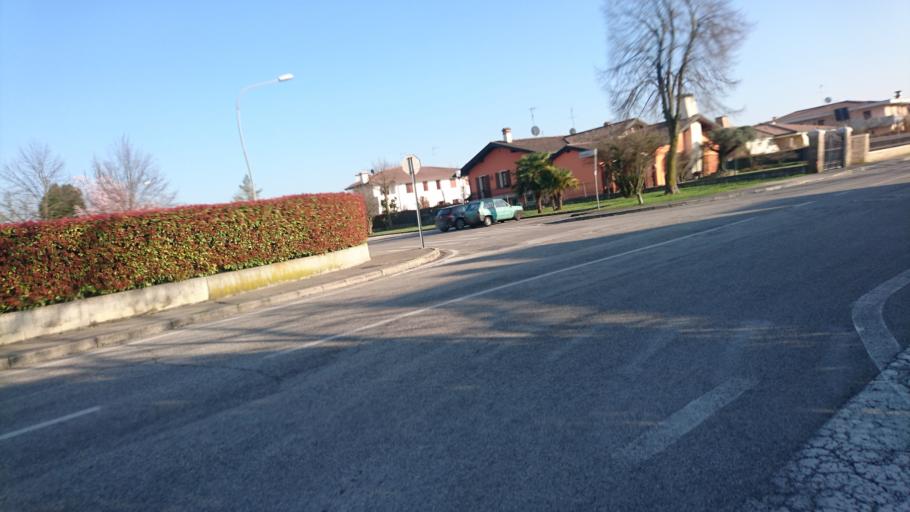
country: IT
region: Veneto
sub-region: Provincia di Padova
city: Vigonza
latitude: 45.4413
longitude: 11.9865
